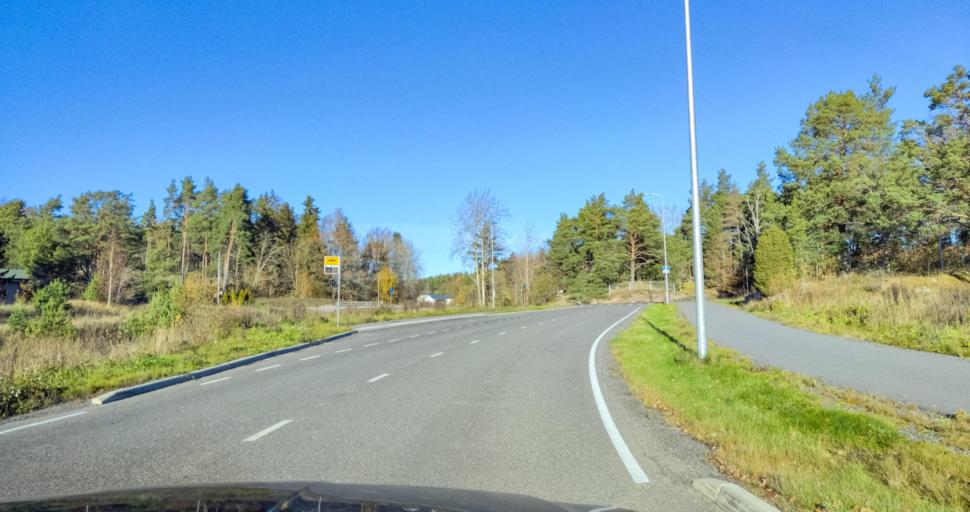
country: FI
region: Varsinais-Suomi
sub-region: Turku
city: Turku
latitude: 60.4071
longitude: 22.2080
